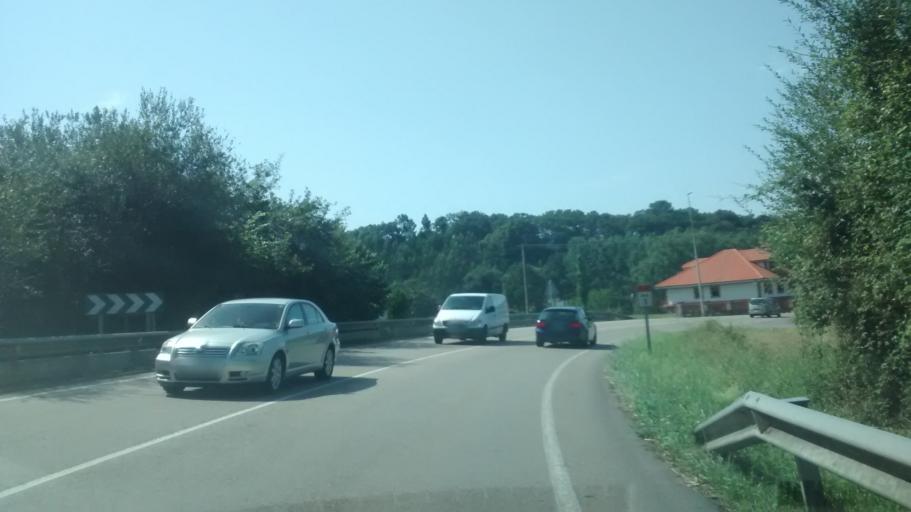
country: ES
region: Cantabria
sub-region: Provincia de Cantabria
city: Hazas de Cesto
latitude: 43.4224
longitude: -3.5686
